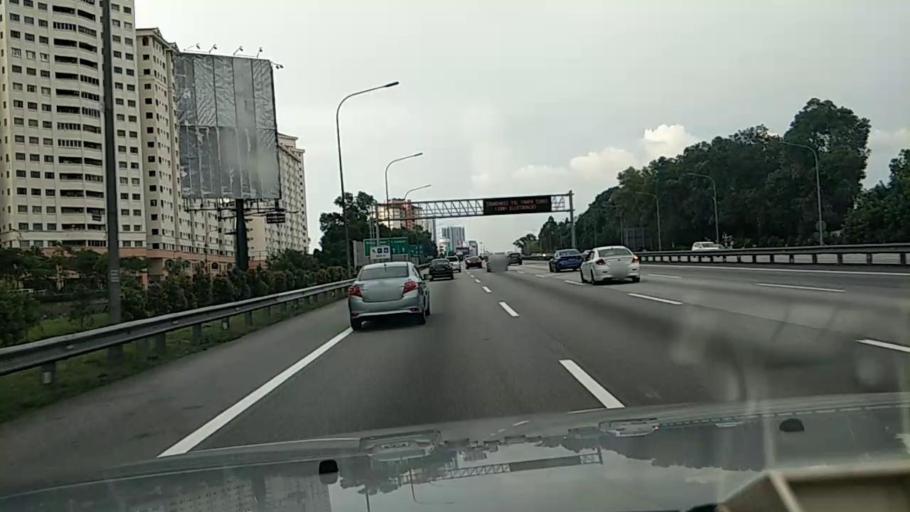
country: MY
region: Selangor
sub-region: Petaling
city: Petaling Jaya
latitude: 3.1131
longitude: 101.5925
